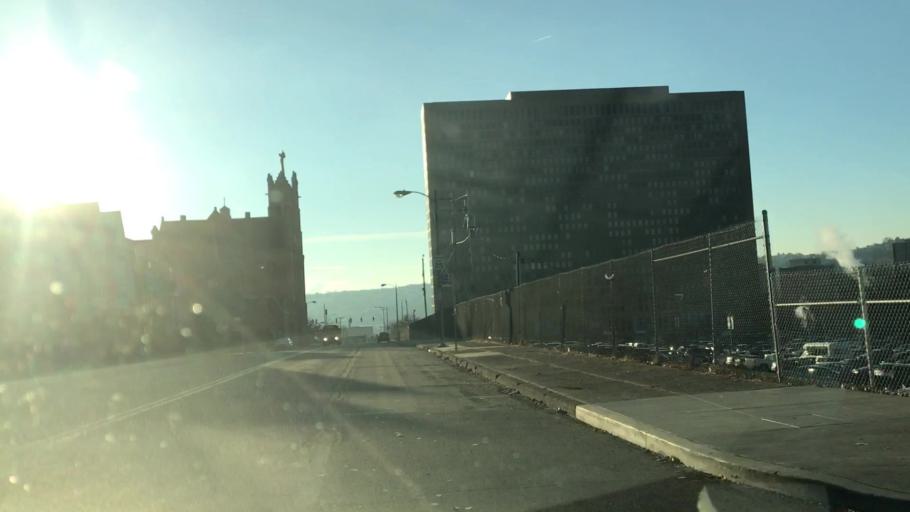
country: US
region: Pennsylvania
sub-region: Allegheny County
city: Pittsburgh
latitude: 40.4426
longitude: -79.9872
